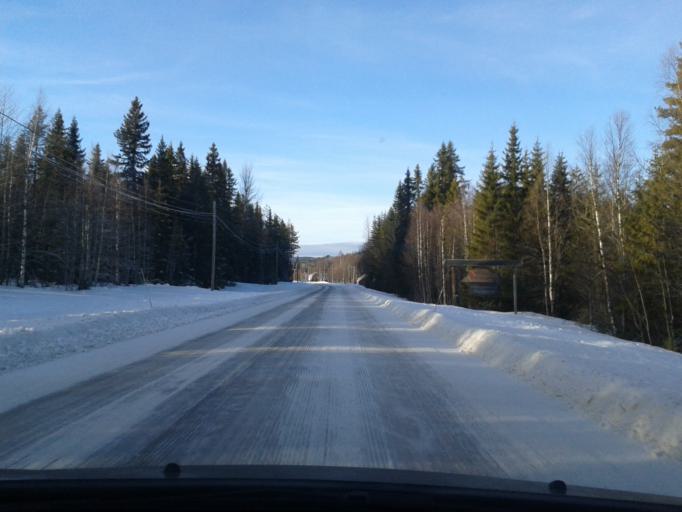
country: SE
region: Vaesterbotten
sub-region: Asele Kommun
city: Asele
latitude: 63.7812
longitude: 17.6626
